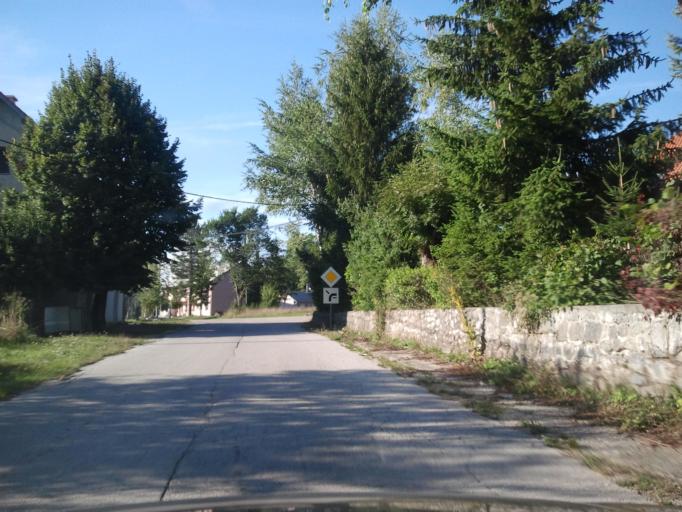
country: HR
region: Zadarska
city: Obrovac
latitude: 44.3608
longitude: 15.6537
